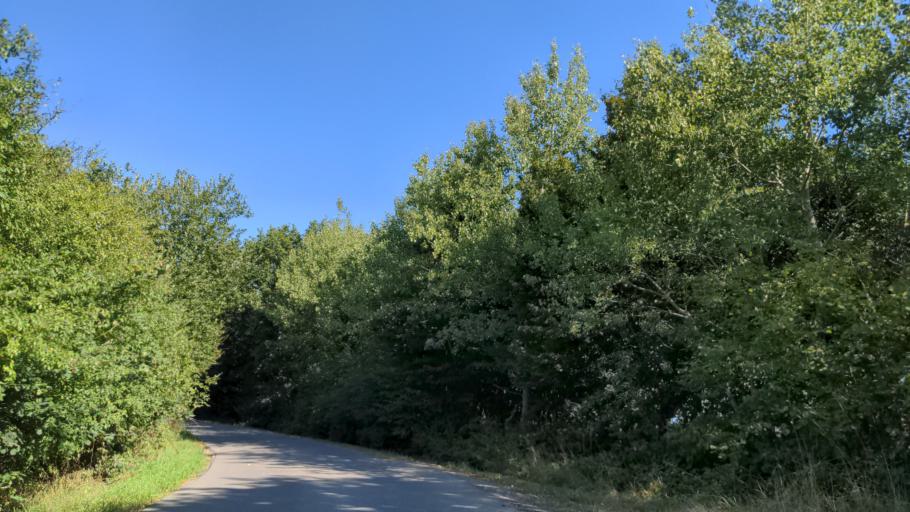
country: DE
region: Schleswig-Holstein
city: Gross Disnack
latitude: 53.7591
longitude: 10.6838
